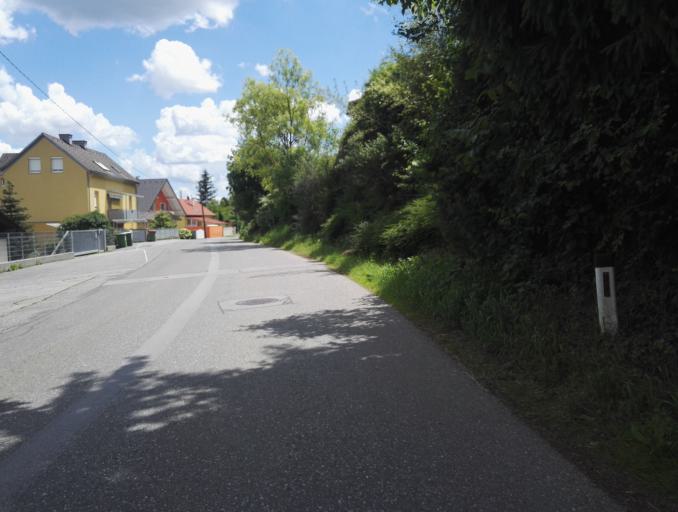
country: AT
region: Styria
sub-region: Graz Stadt
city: Goesting
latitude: 47.0897
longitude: 15.3988
